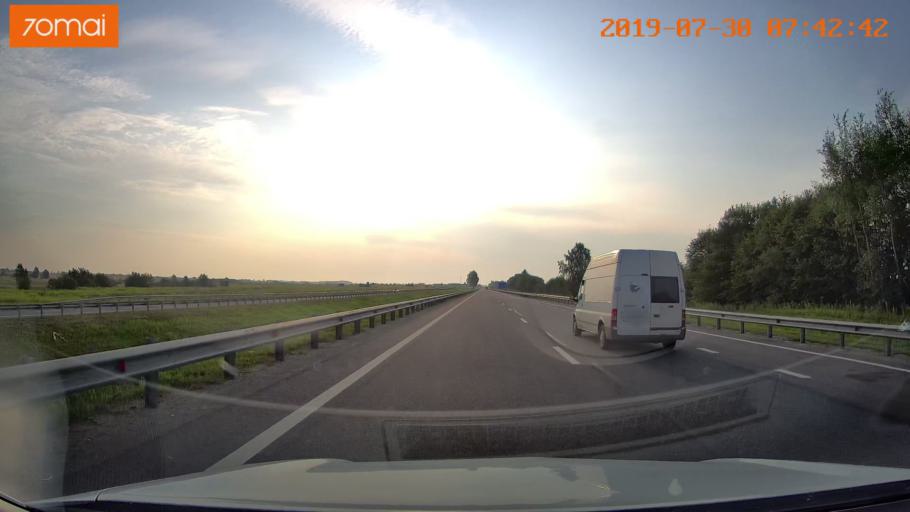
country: RU
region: Kaliningrad
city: Gvardeysk
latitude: 54.6481
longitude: 21.2860
